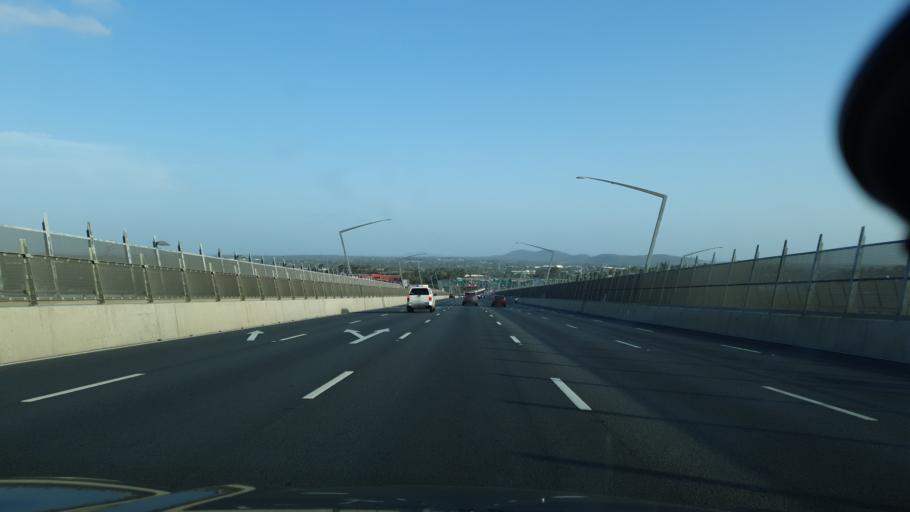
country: AU
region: Queensland
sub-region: Brisbane
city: Cannon Hill
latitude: -27.4474
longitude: 153.1027
